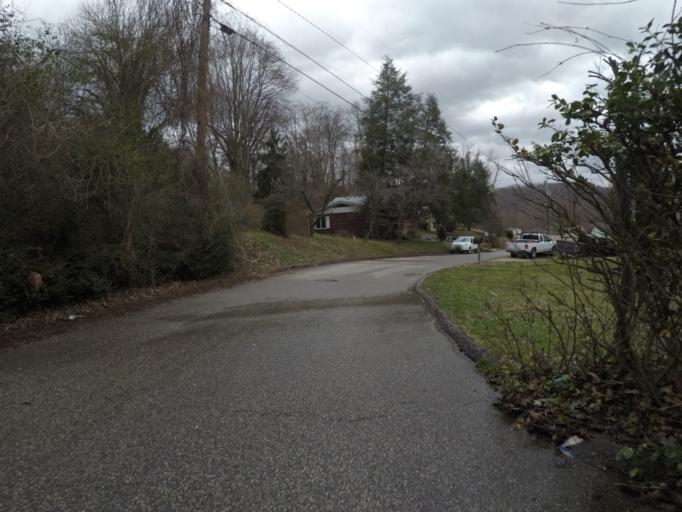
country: US
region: West Virginia
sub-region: Cabell County
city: Pea Ridge
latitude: 38.4085
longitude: -82.3802
